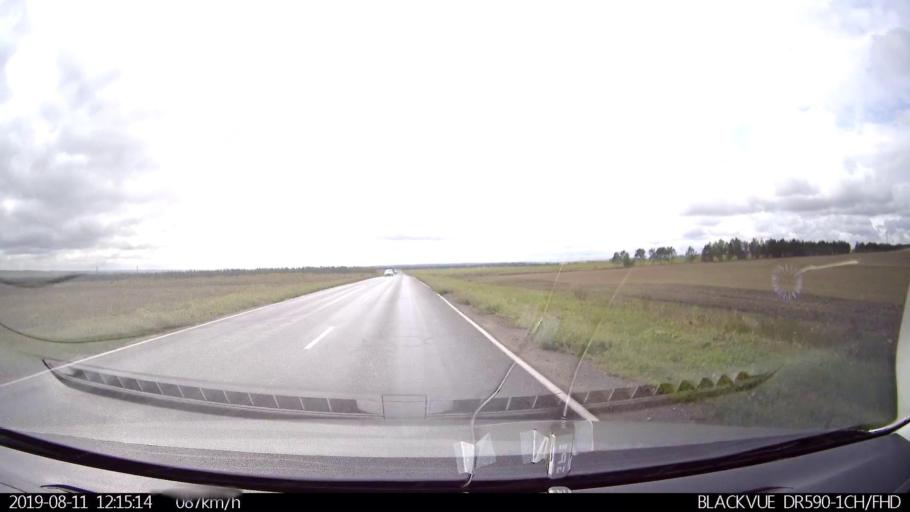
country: RU
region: Ulyanovsk
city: Ignatovka
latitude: 53.9441
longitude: 47.9706
